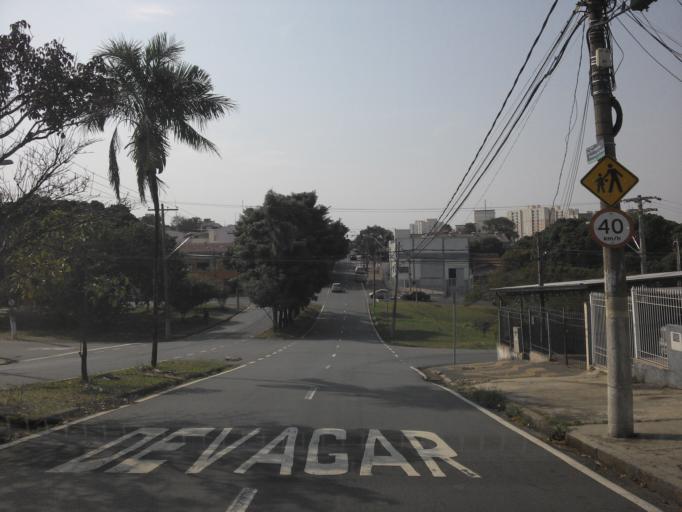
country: BR
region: Sao Paulo
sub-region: Campinas
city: Campinas
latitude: -22.9111
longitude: -47.0855
